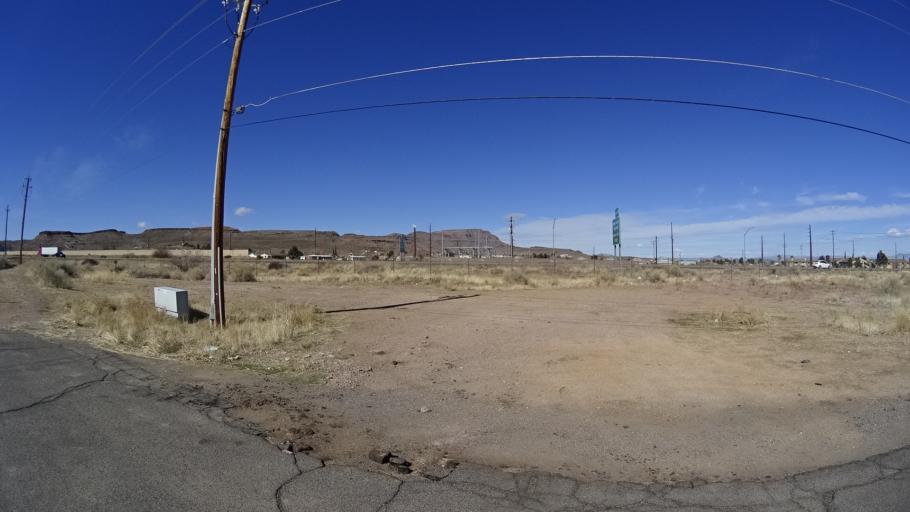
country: US
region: Arizona
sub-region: Mohave County
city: Kingman
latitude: 35.2149
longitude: -114.0434
